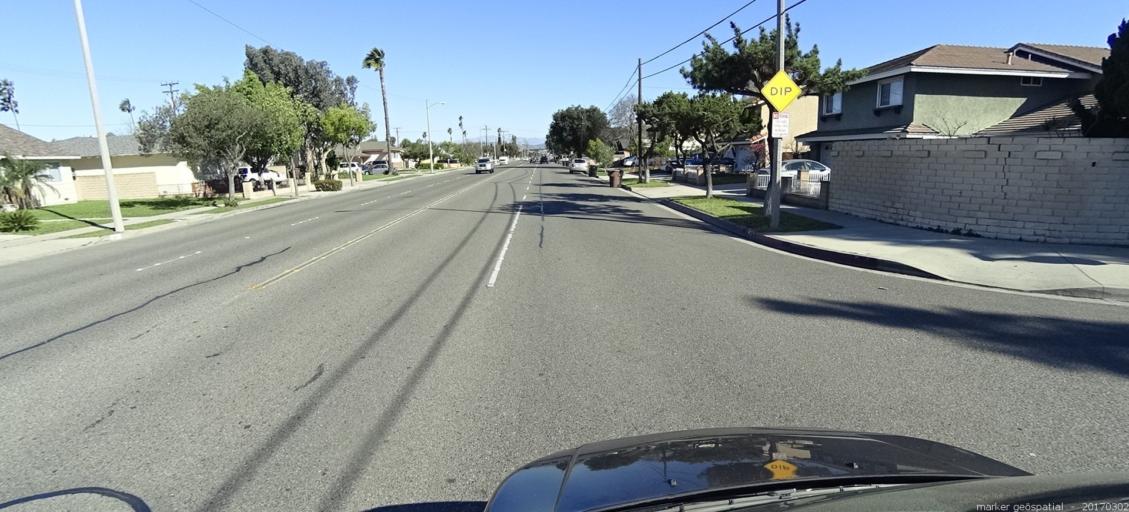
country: US
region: California
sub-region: Orange County
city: Placentia
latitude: 33.8417
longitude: -117.8804
